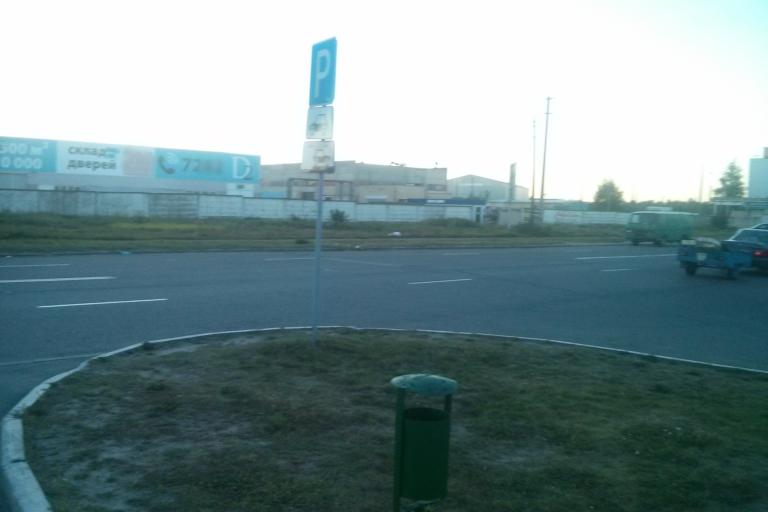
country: BY
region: Minsk
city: Vyaliki Trastsyanets
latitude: 53.8380
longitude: 27.6836
